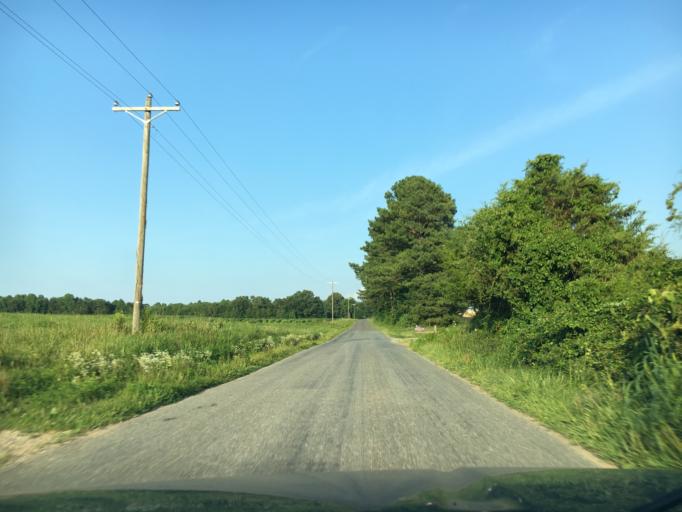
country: US
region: Virginia
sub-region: Pittsylvania County
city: Gretna
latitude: 36.8418
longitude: -79.1951
